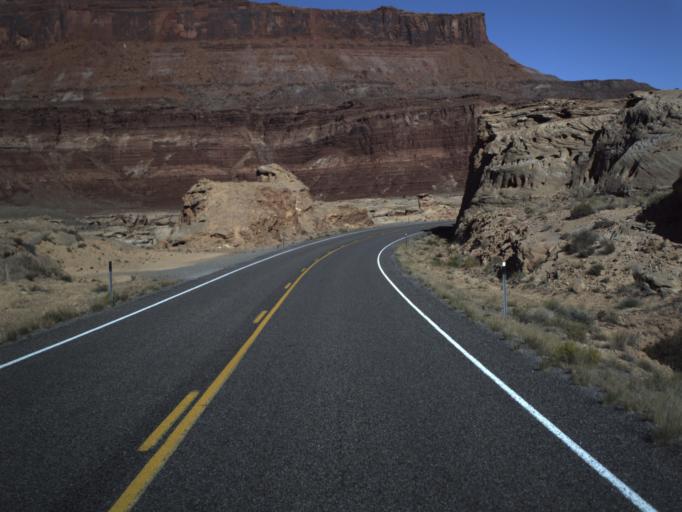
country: US
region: Utah
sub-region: San Juan County
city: Blanding
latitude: 37.9118
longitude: -110.3868
